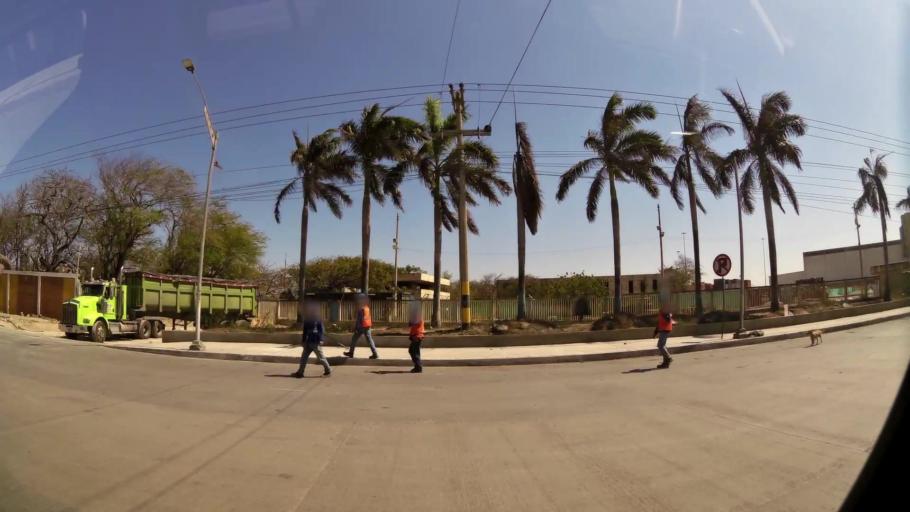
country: CO
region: Atlantico
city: Barranquilla
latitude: 10.9706
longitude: -74.7649
